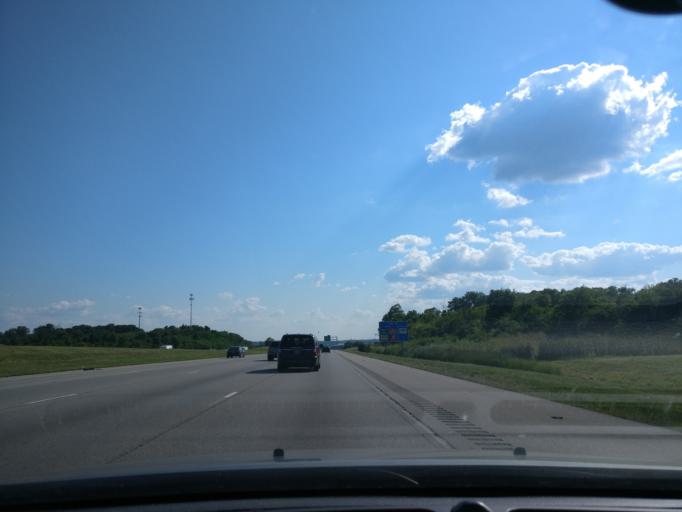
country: US
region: Ohio
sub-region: Warren County
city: Springboro
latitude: 39.5732
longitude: -84.2584
